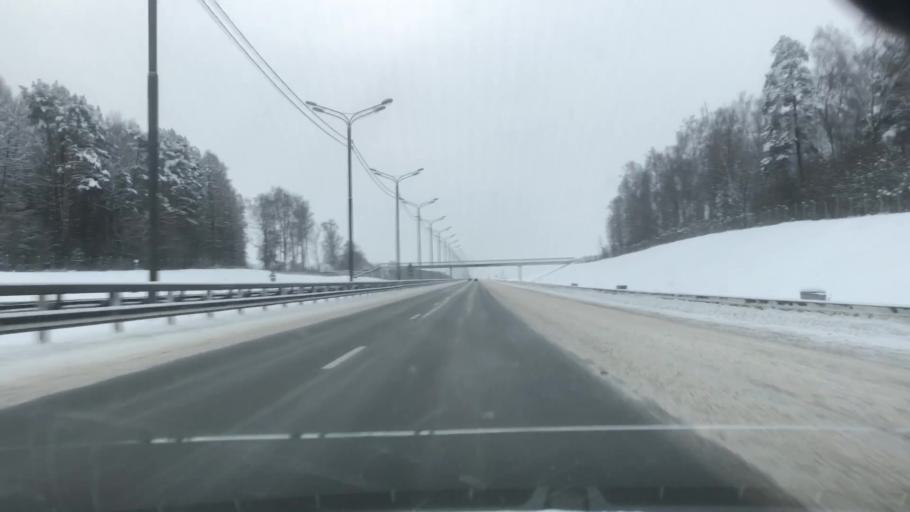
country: RU
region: Moskovskaya
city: Barybino
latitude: 55.2713
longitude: 37.8668
